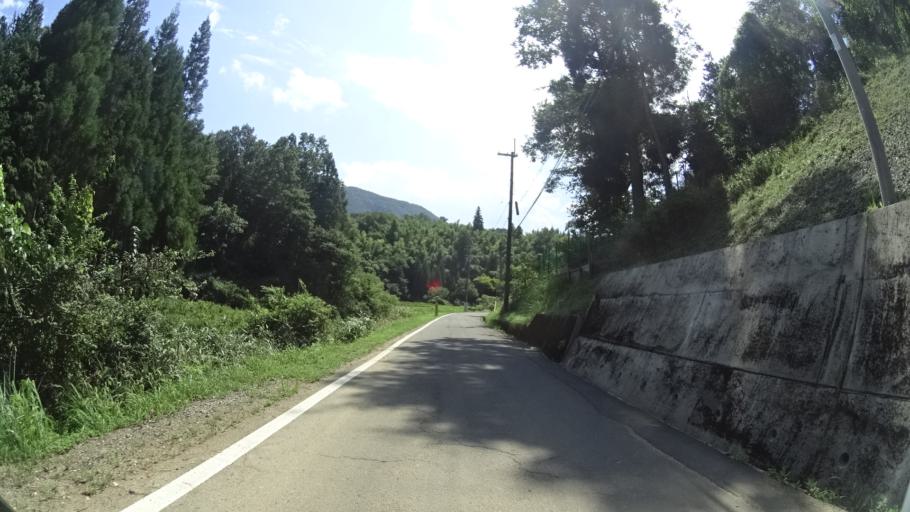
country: JP
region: Kyoto
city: Maizuru
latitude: 35.3779
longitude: 135.3515
